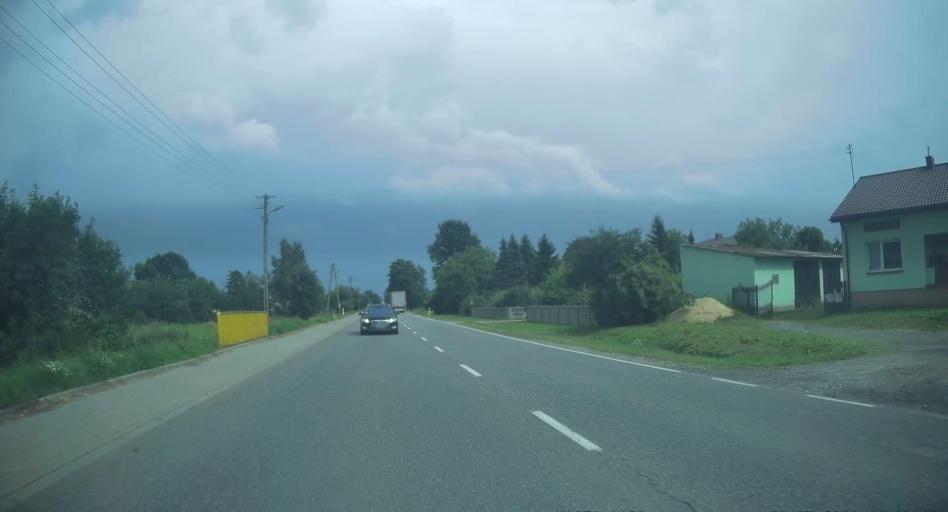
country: PL
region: Lodz Voivodeship
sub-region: Powiat skierniewicki
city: Gluchow
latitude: 51.7733
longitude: 20.1355
